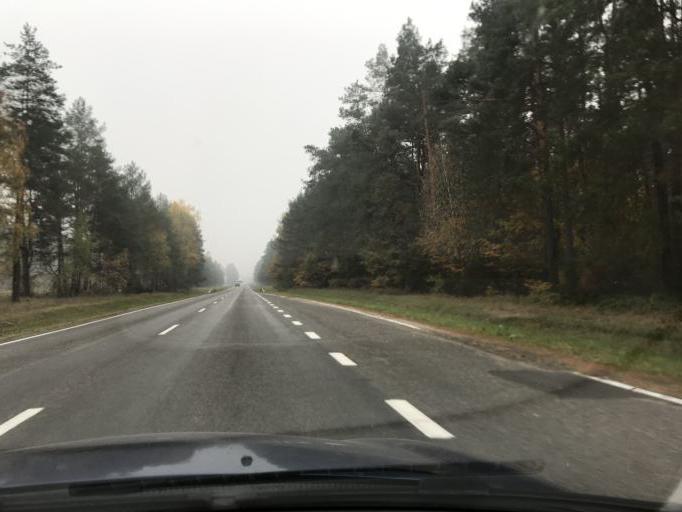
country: BY
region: Grodnenskaya
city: Hrodna
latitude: 53.7956
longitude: 23.8560
